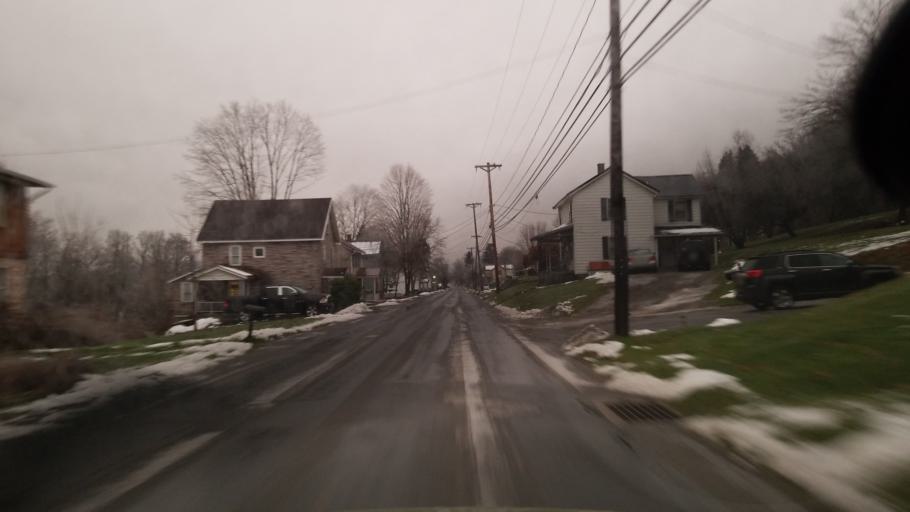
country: US
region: Pennsylvania
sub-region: Clearfield County
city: Clearfield
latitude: 41.0382
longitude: -78.4540
